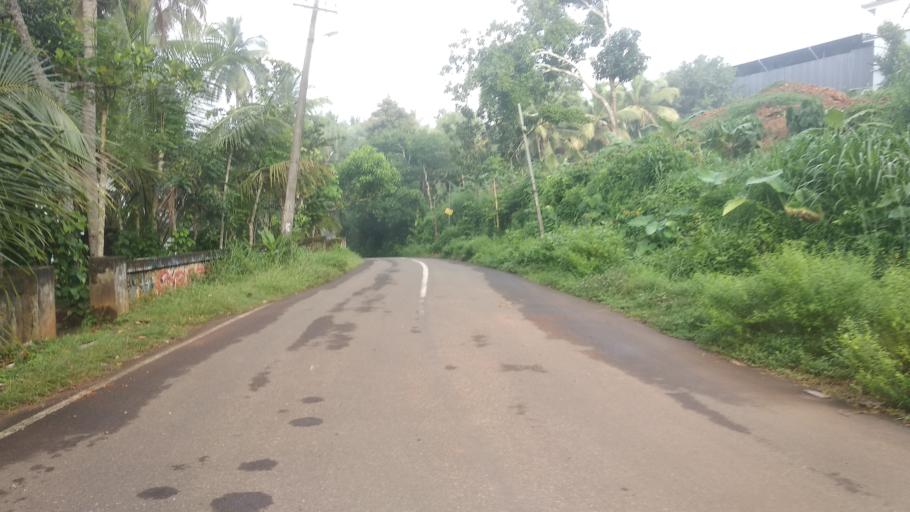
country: IN
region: Kerala
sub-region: Malappuram
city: Malappuram
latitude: 10.9897
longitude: 76.0471
